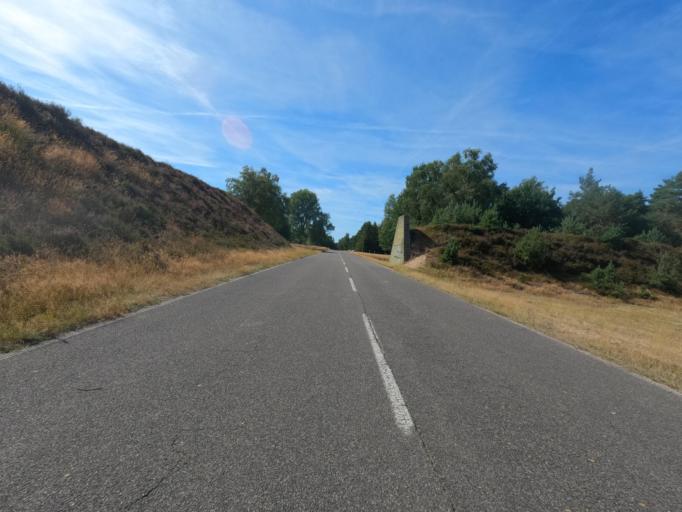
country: DE
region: North Rhine-Westphalia
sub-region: Regierungsbezirk Dusseldorf
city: Bruggen
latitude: 51.2626
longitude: 6.1523
